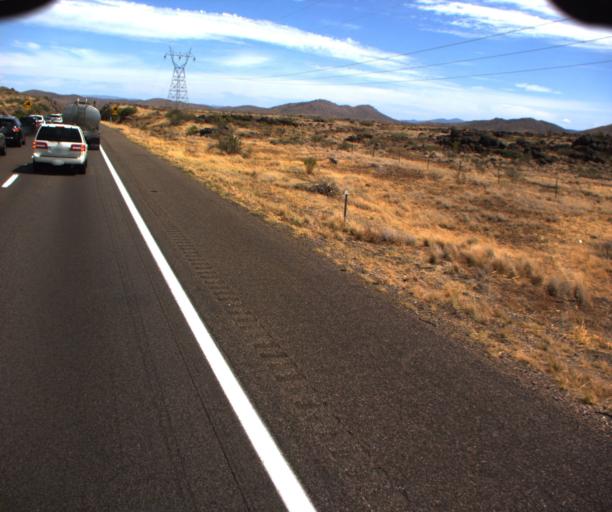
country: US
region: Arizona
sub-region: Yavapai County
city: Cordes Lakes
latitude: 34.2225
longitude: -112.1107
